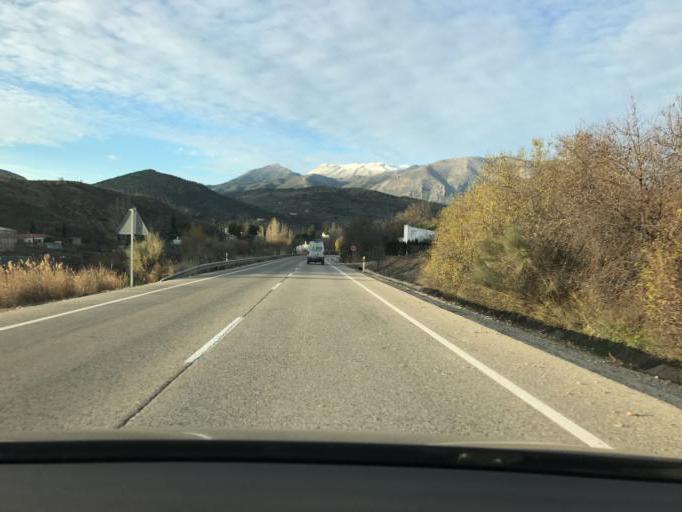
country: ES
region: Andalusia
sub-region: Provincia de Jaen
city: Huelma
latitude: 37.6448
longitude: -3.4181
